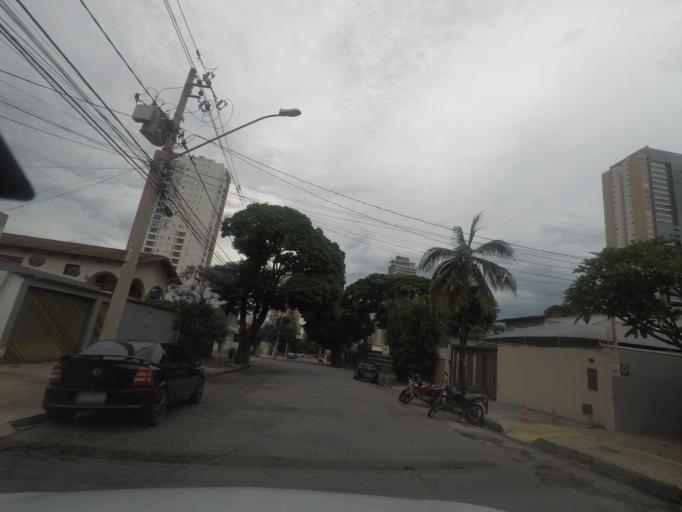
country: BR
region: Goias
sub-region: Goiania
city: Goiania
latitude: -16.6936
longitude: -49.2687
